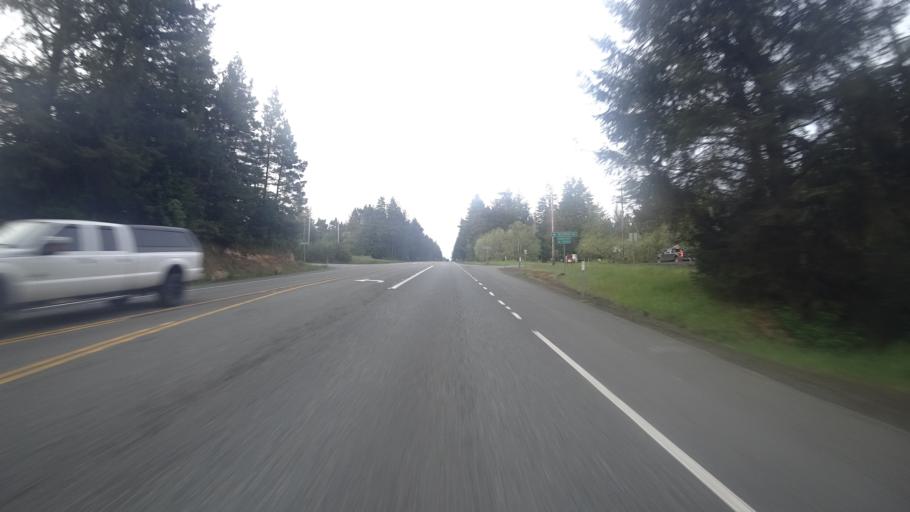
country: US
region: Oregon
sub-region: Coos County
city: Lakeside
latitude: 43.5242
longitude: -124.2164
